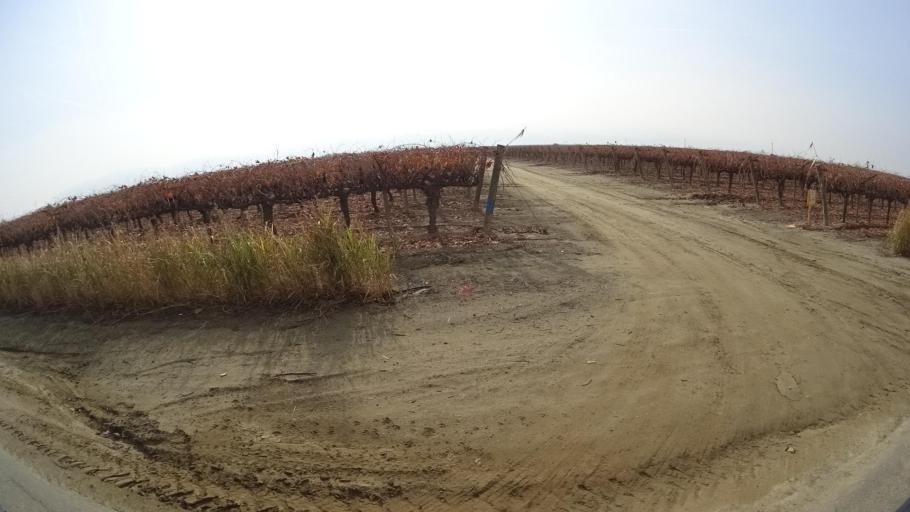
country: US
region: California
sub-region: Kern County
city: Greenfield
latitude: 35.0767
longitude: -119.0895
